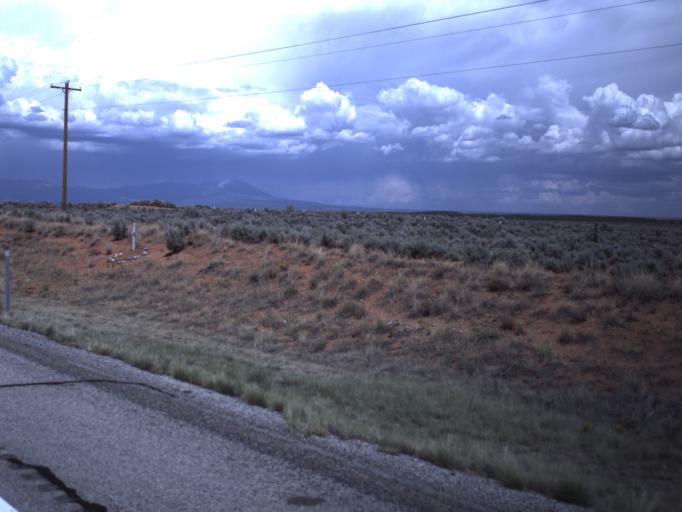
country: US
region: Utah
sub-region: San Juan County
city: Blanding
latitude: 37.5001
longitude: -109.4852
